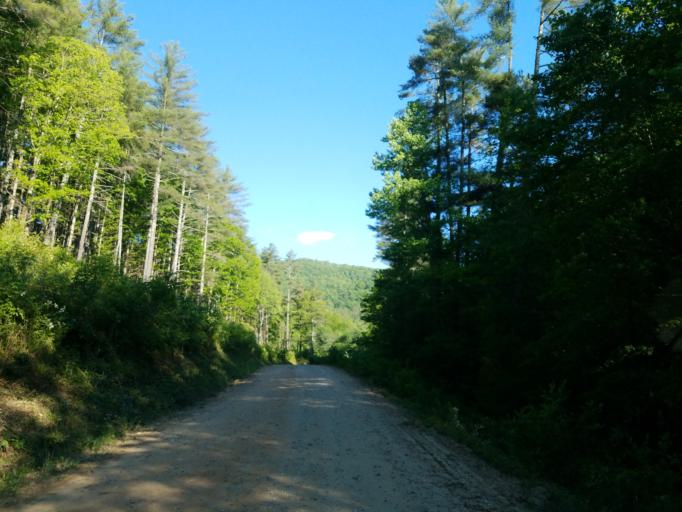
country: US
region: Georgia
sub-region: Fannin County
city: Blue Ridge
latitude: 34.7281
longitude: -84.1529
